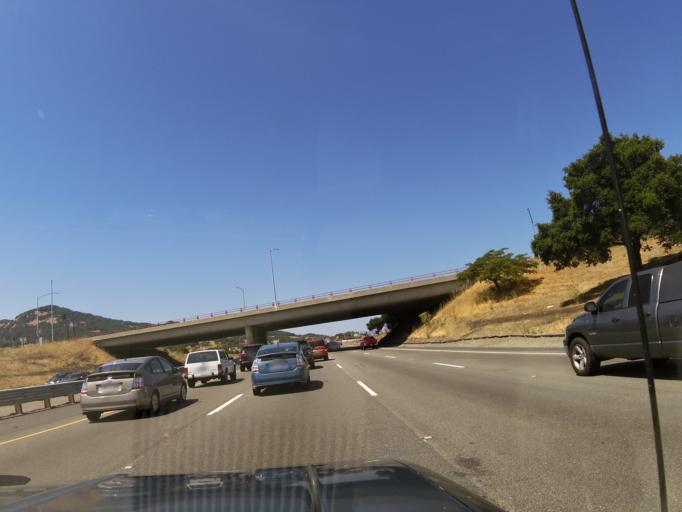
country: US
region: California
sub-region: Marin County
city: Novato
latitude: 38.1169
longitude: -122.5649
